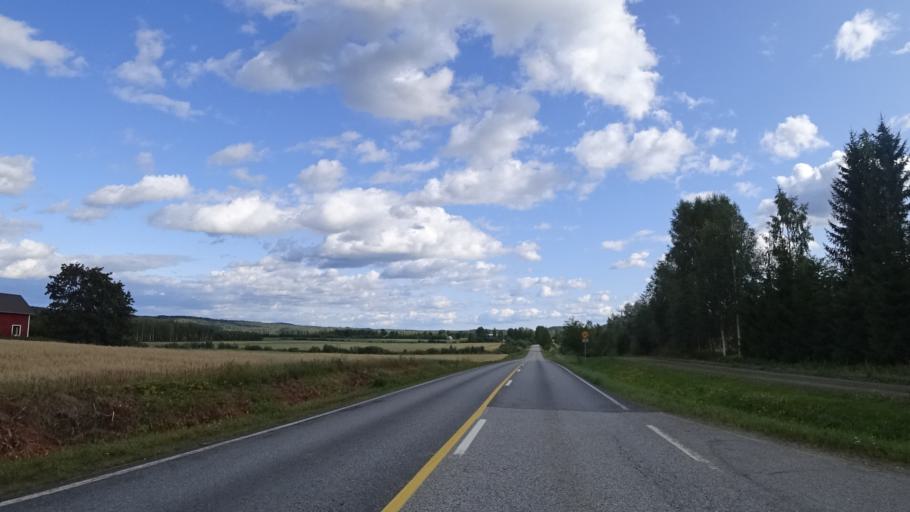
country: RU
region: Republic of Karelia
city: Vyartsilya
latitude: 62.2127
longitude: 30.6000
